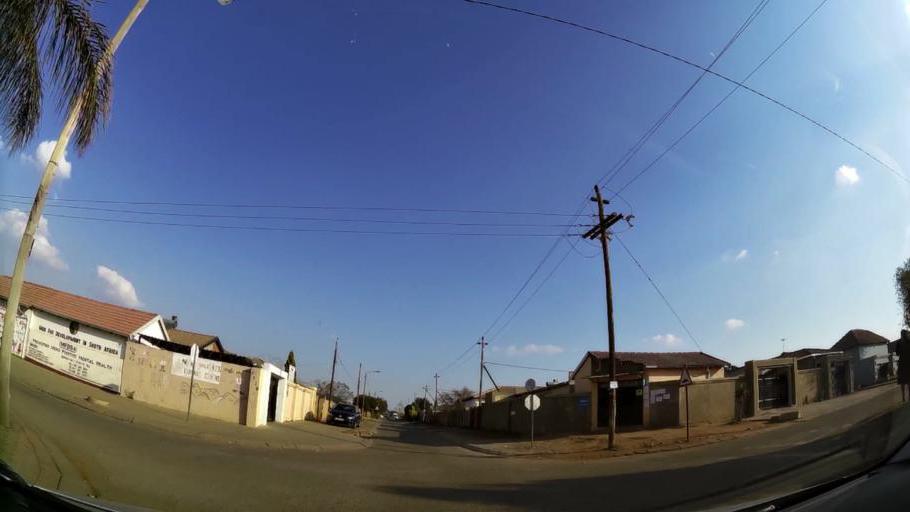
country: ZA
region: Gauteng
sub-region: Ekurhuleni Metropolitan Municipality
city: Tembisa
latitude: -25.9535
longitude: 28.2027
